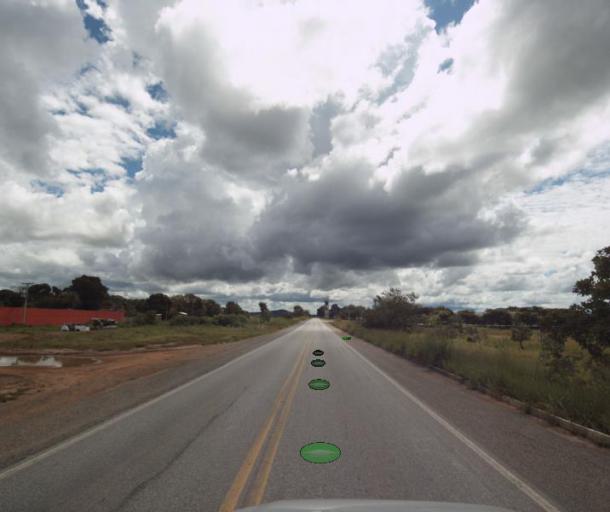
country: BR
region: Goias
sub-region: Uruacu
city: Uruacu
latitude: -14.2849
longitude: -49.1493
